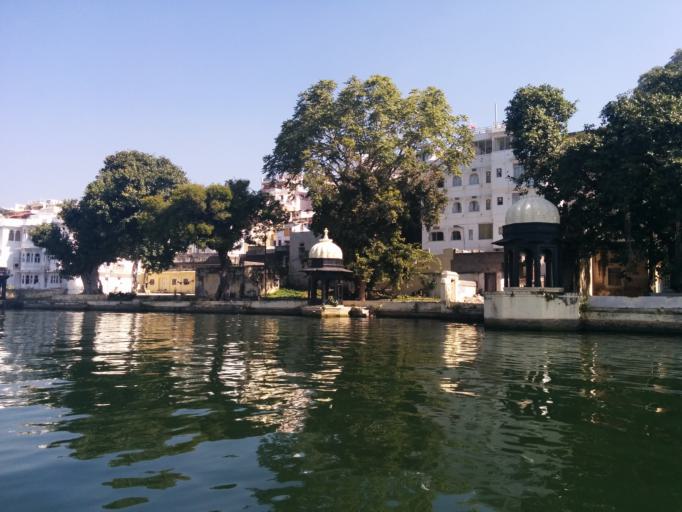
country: IN
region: Rajasthan
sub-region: Udaipur
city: Udaipur
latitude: 24.5776
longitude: 73.6820
